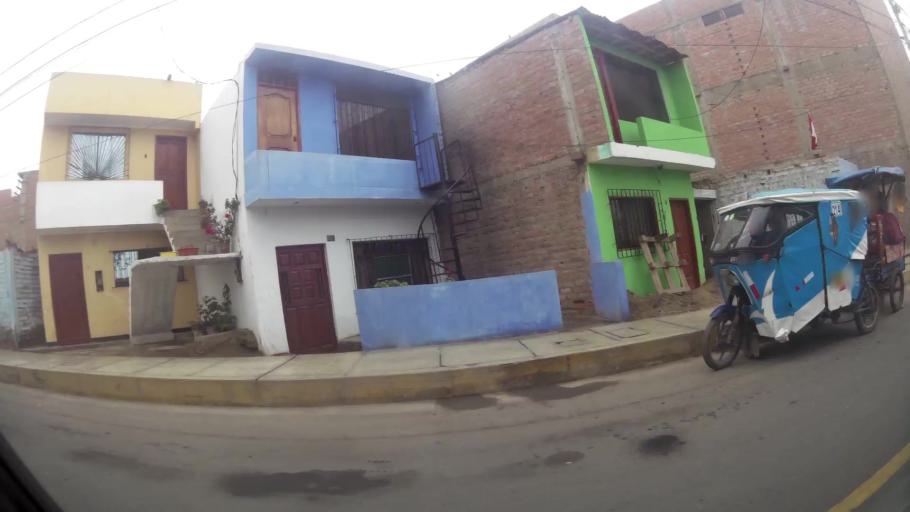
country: PE
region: Lima
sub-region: Provincia de Huaral
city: Chancay
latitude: -11.5611
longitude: -77.2729
